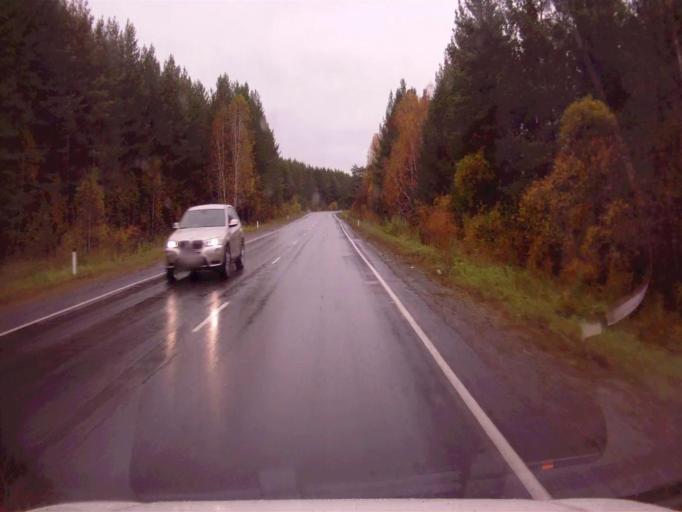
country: RU
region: Chelyabinsk
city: Verkhniy Ufaley
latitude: 56.0120
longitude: 60.3172
